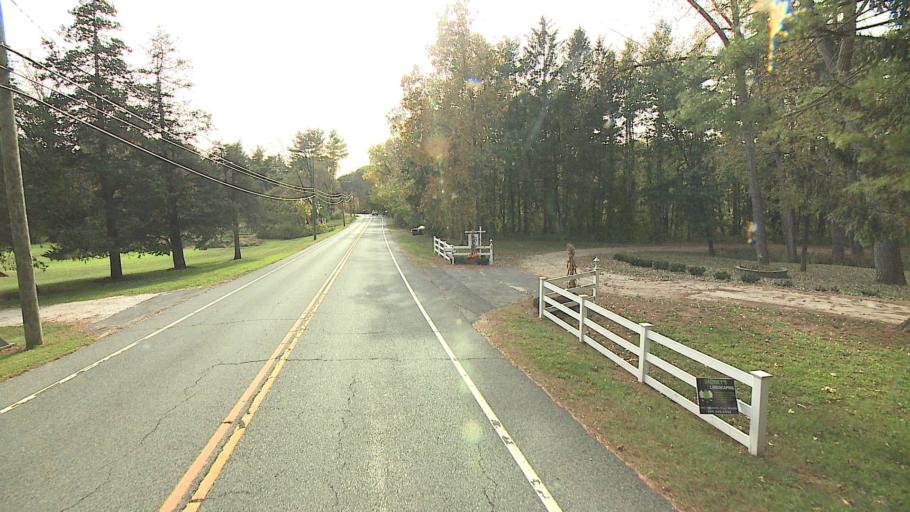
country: US
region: Connecticut
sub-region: Litchfield County
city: Canaan
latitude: 42.0192
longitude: -73.3490
